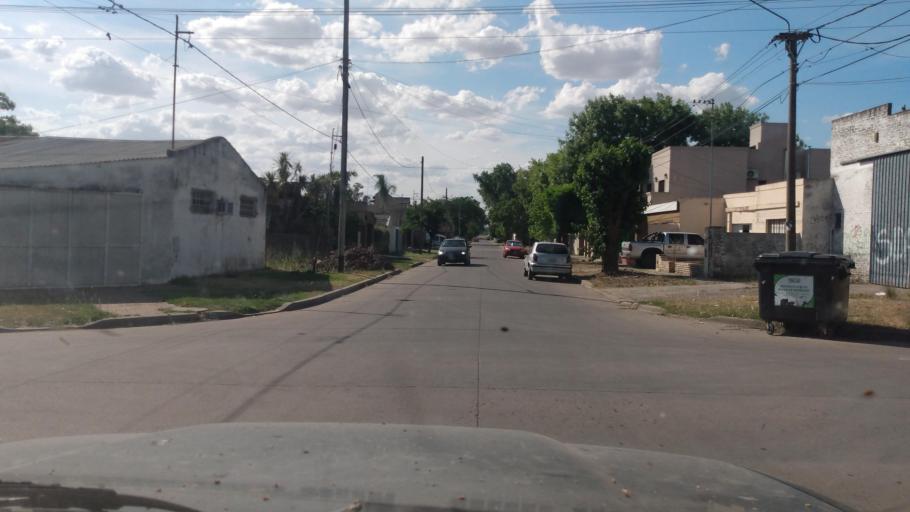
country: AR
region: Buenos Aires
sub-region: Partido de Lujan
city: Lujan
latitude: -34.5554
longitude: -59.1086
